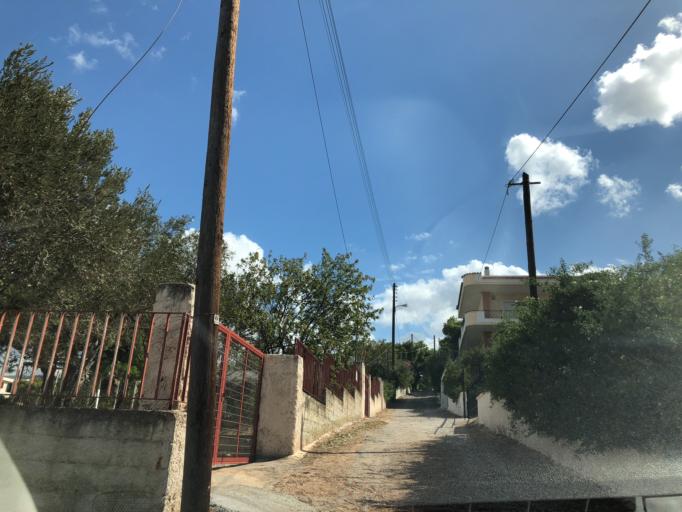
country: GR
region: Attica
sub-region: Nomarchia Anatolikis Attikis
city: Agia Marina
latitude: 37.8222
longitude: 23.8599
